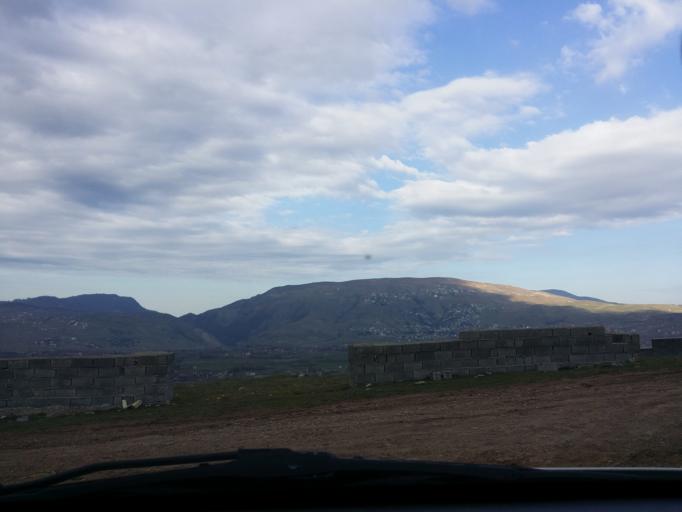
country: IR
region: Mazandaran
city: `Abbasabad
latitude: 36.5006
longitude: 51.1801
